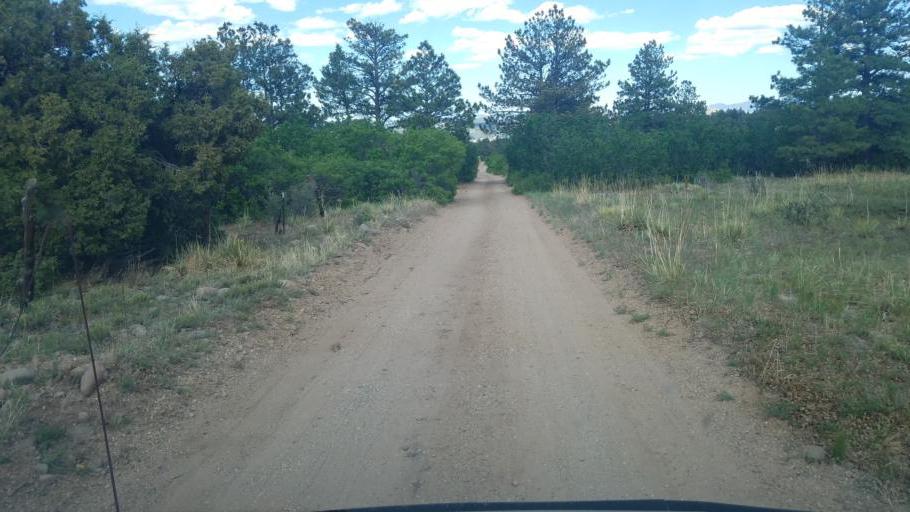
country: US
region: Colorado
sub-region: Custer County
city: Westcliffe
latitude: 38.2218
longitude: -105.6136
